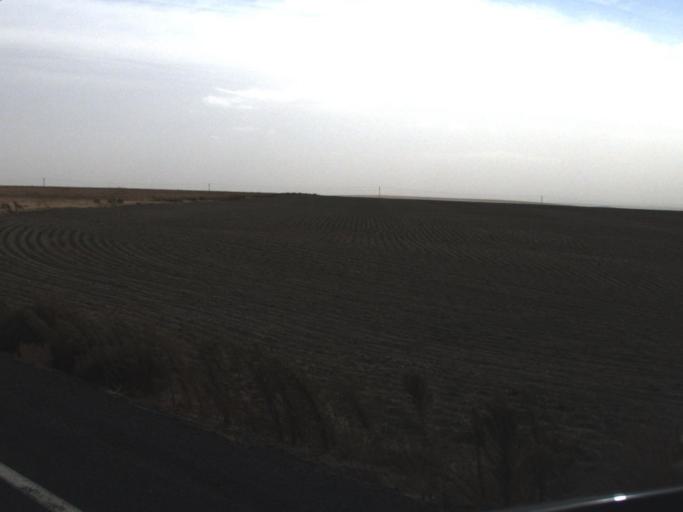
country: US
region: Washington
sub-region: Adams County
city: Ritzville
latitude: 47.4418
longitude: -118.7313
